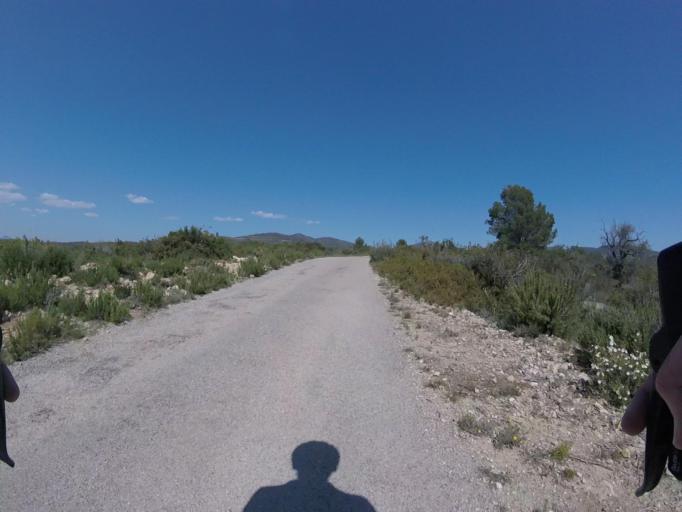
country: ES
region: Valencia
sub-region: Provincia de Castello
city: Sierra-Engarceran
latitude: 40.2269
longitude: -0.0228
